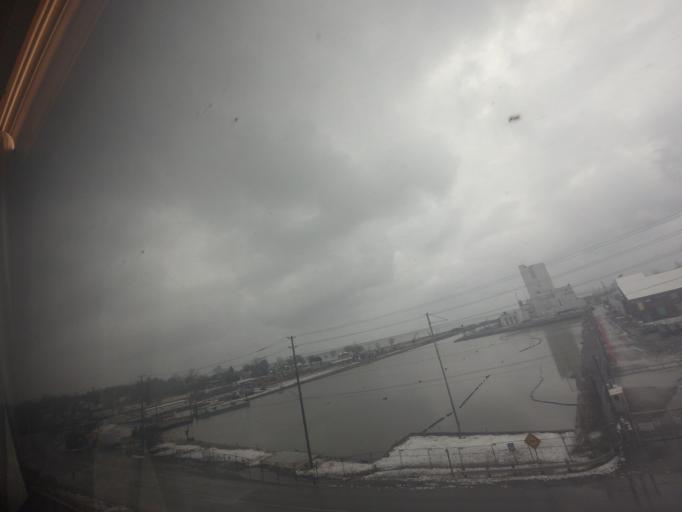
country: CA
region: Ontario
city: Cobourg
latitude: 43.9457
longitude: -78.2955
